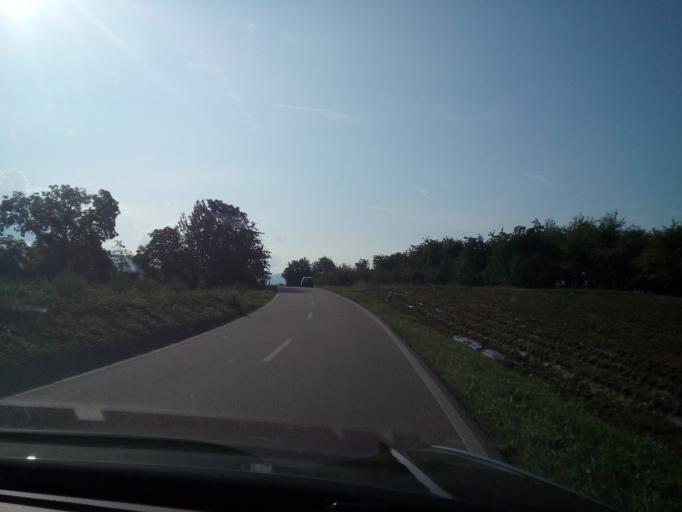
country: DE
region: Baden-Wuerttemberg
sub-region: Freiburg Region
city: Renchen
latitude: 48.5789
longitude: 8.0217
